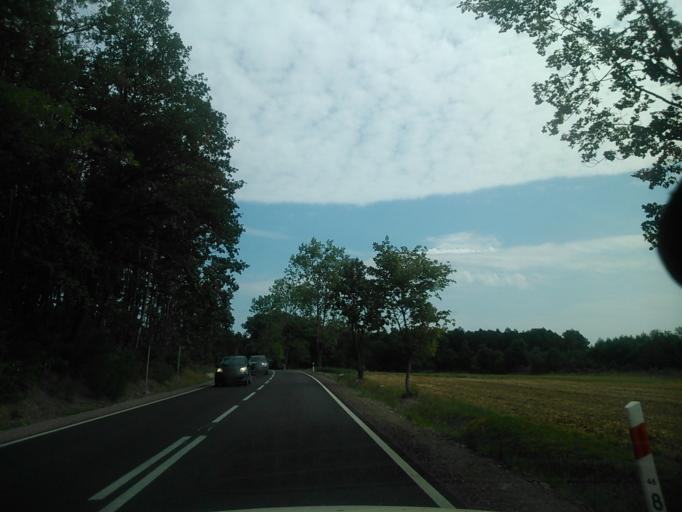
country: PL
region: Warmian-Masurian Voivodeship
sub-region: Powiat dzialdowski
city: Dzialdowo
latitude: 53.2349
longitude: 20.0481
